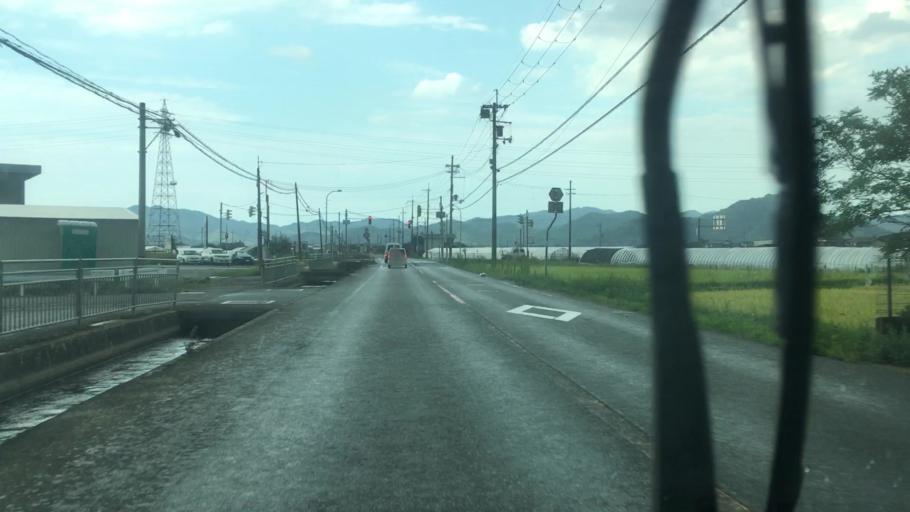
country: JP
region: Hyogo
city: Toyooka
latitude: 35.5025
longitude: 134.8207
